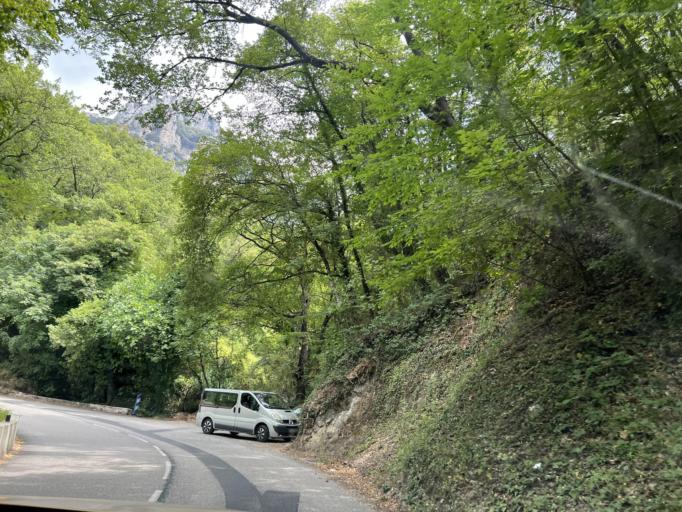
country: FR
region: Provence-Alpes-Cote d'Azur
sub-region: Departement des Alpes-Maritimes
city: Le Rouret
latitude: 43.7202
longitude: 6.9942
